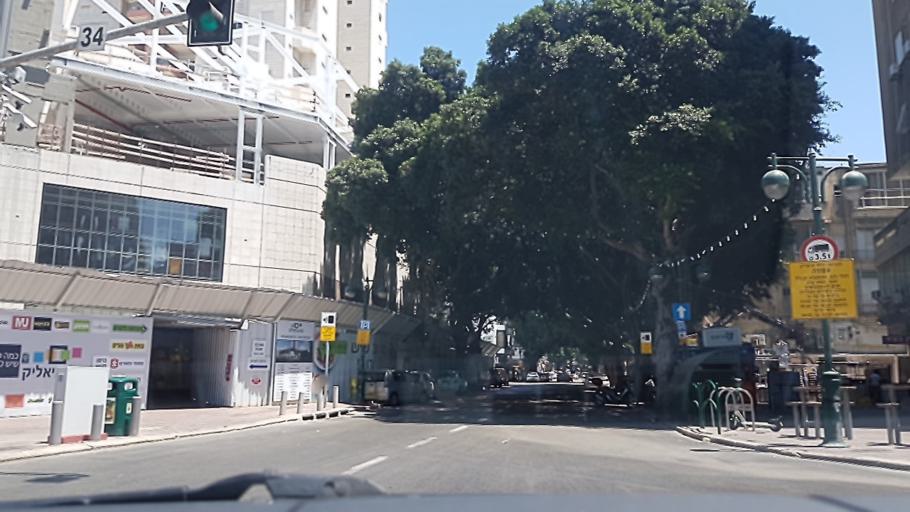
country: IL
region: Tel Aviv
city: Ramat Gan
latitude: 32.0857
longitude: 34.8107
